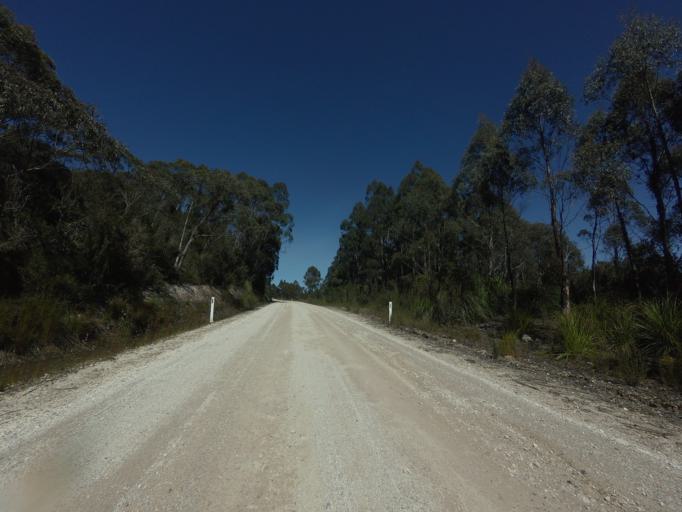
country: AU
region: Tasmania
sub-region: Huon Valley
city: Geeveston
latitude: -42.9083
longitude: 146.3653
